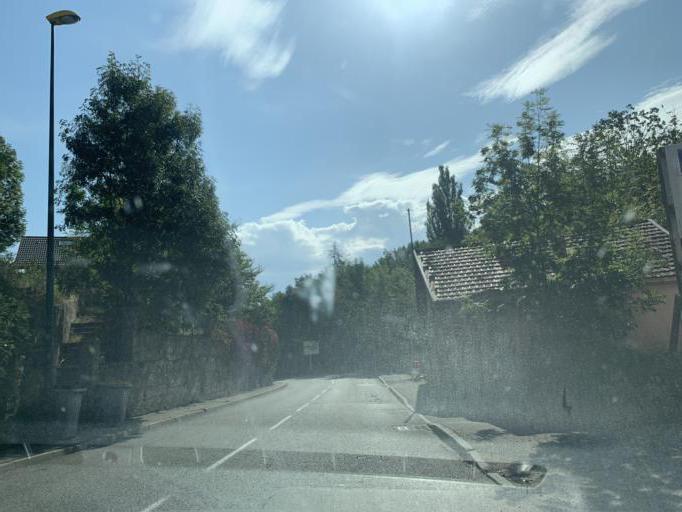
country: FR
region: Rhone-Alpes
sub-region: Departement de l'Ain
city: Bellegarde-sur-Valserine
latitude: 46.1091
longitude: 5.8153
